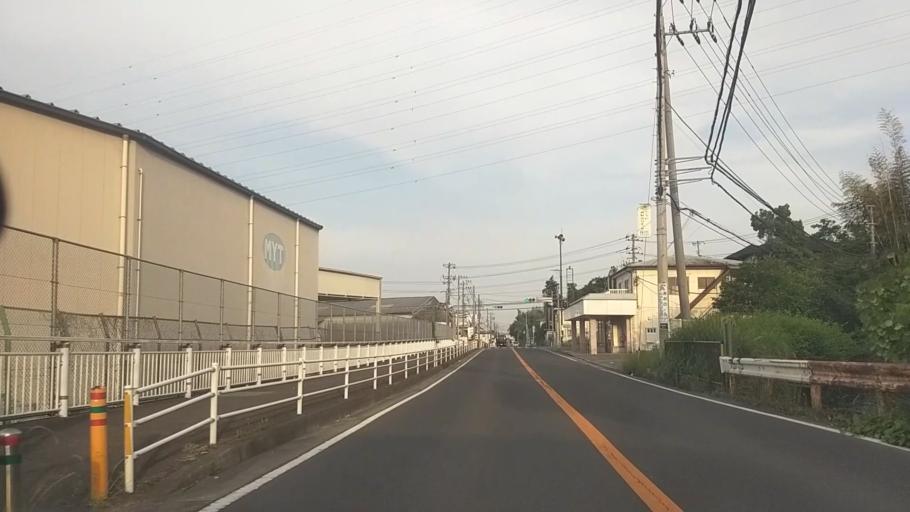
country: JP
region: Kanagawa
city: Odawara
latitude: 35.2834
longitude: 139.1428
